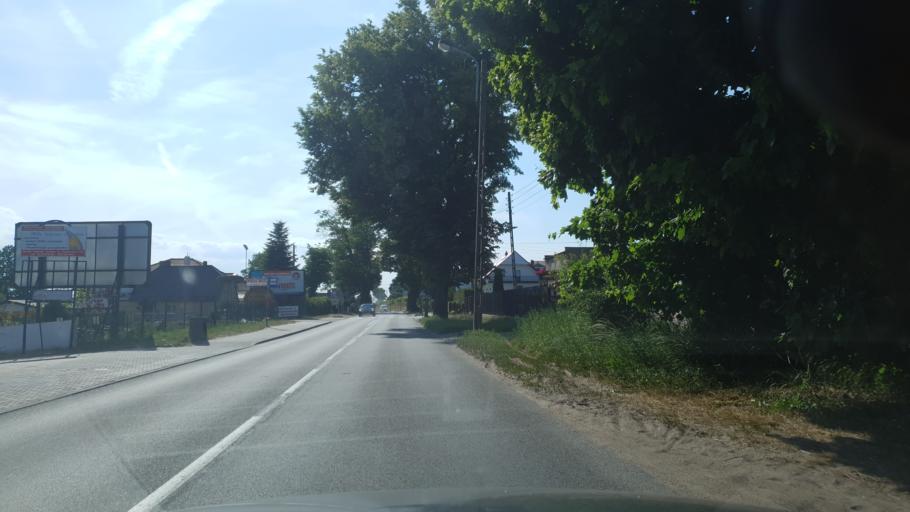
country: PL
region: Pomeranian Voivodeship
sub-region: Powiat kartuski
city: Chwaszczyno
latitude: 54.4417
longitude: 18.4533
